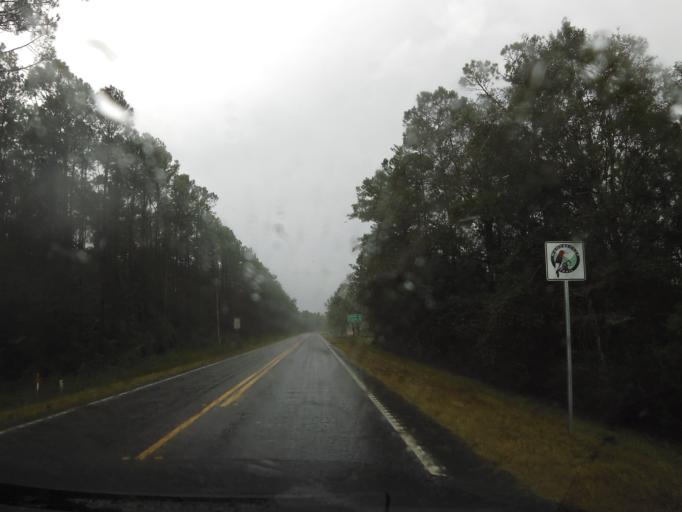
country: US
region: Florida
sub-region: Baker County
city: Macclenny
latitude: 30.3684
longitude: -82.1379
